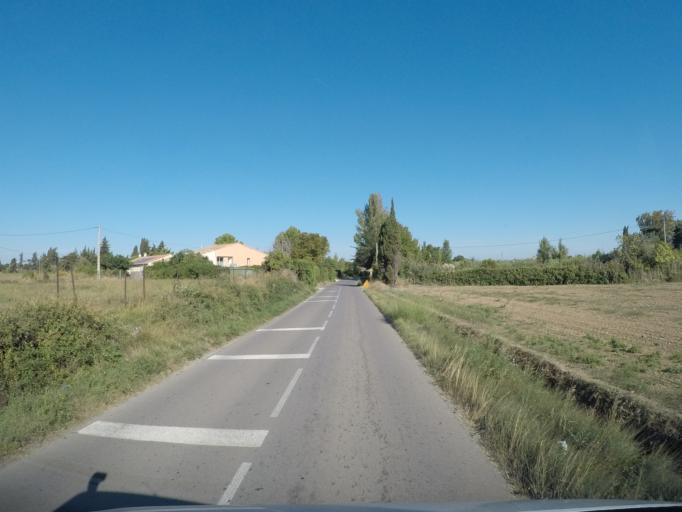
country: FR
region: Languedoc-Roussillon
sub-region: Departement de l'Aude
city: Narbonne
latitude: 43.1650
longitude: 3.0107
